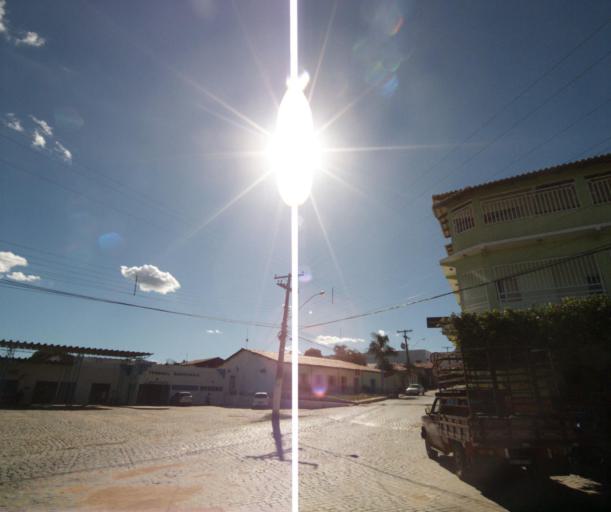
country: BR
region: Bahia
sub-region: Carinhanha
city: Carinhanha
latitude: -14.1819
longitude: -44.5369
